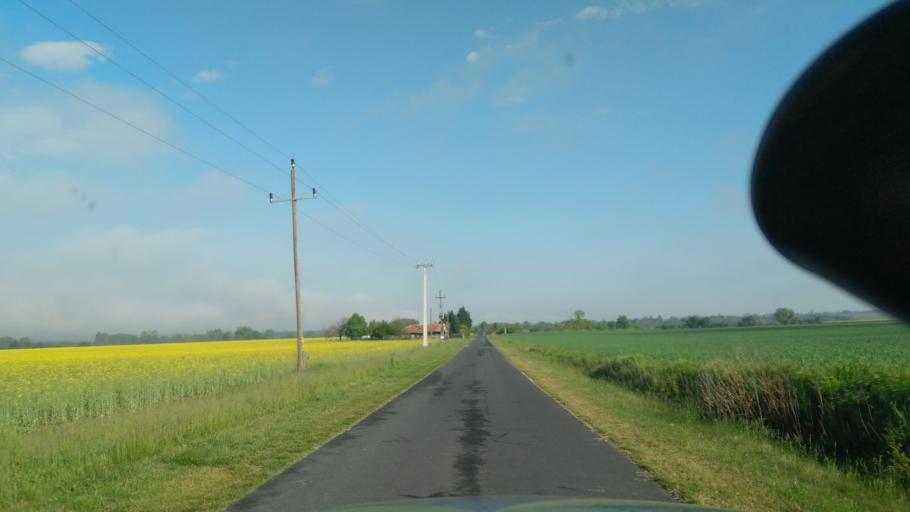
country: HU
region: Zala
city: Sarmellek
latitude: 46.7351
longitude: 17.1486
